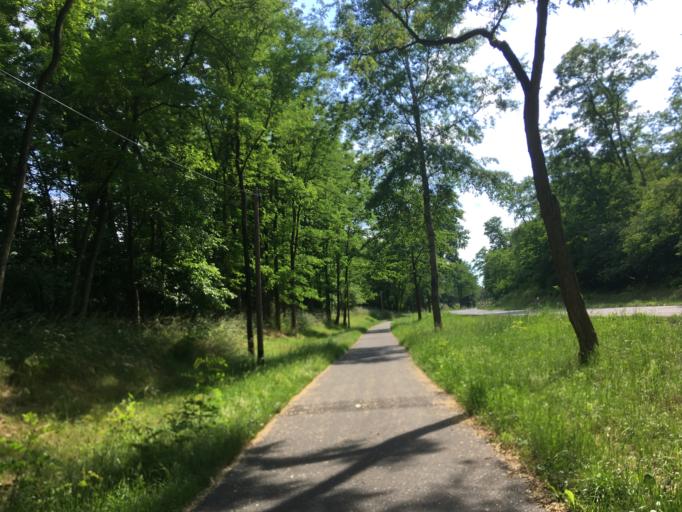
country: DE
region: Brandenburg
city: Furstenwalde
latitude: 52.3950
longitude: 14.0935
